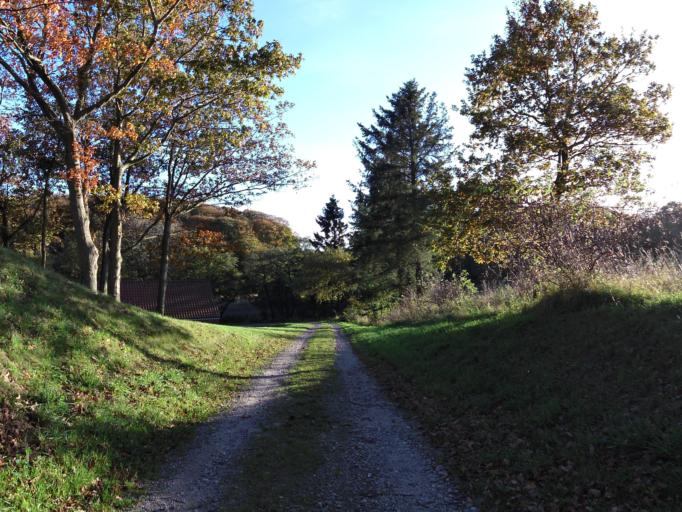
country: DK
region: Central Jutland
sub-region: Arhus Kommune
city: Framlev
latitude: 56.1267
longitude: 10.0286
